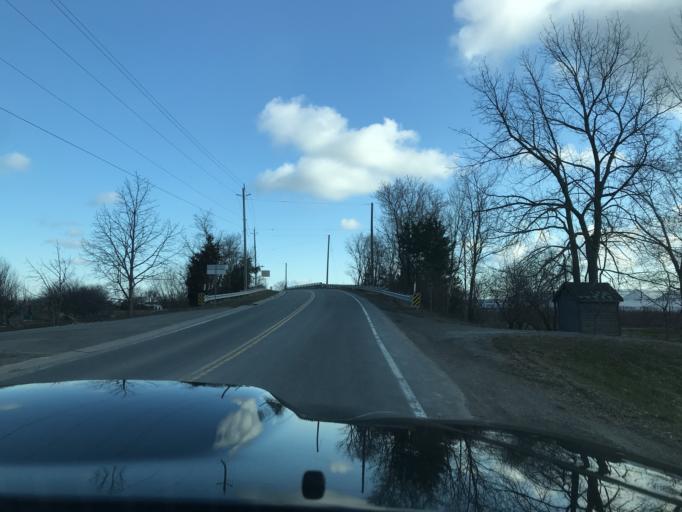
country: CA
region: Ontario
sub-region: Regional Municipality of Niagara
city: St. Catharines
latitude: 43.1541
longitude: -79.3077
